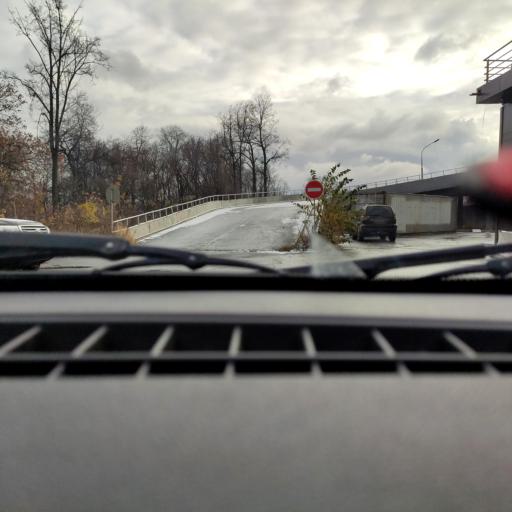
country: RU
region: Bashkortostan
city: Ufa
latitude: 54.7255
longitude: 56.0221
